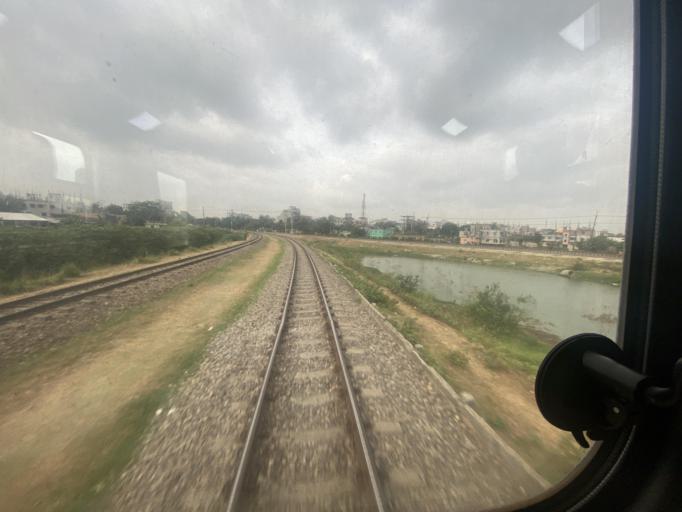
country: BD
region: Dhaka
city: Tungi
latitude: 23.9077
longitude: 90.4101
